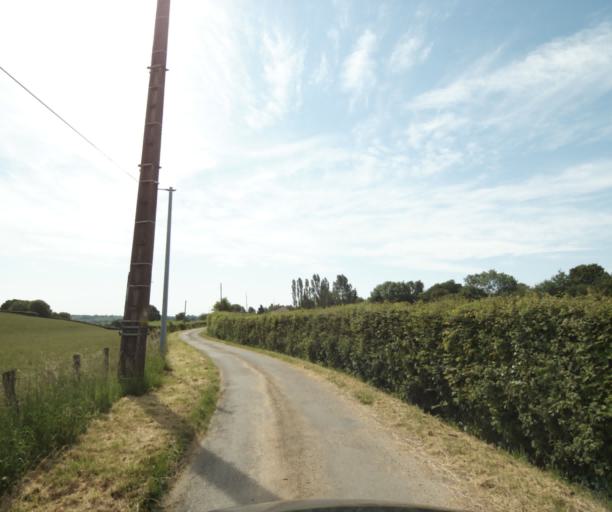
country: FR
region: Bourgogne
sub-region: Departement de Saone-et-Loire
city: Paray-le-Monial
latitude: 46.5403
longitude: 4.1241
